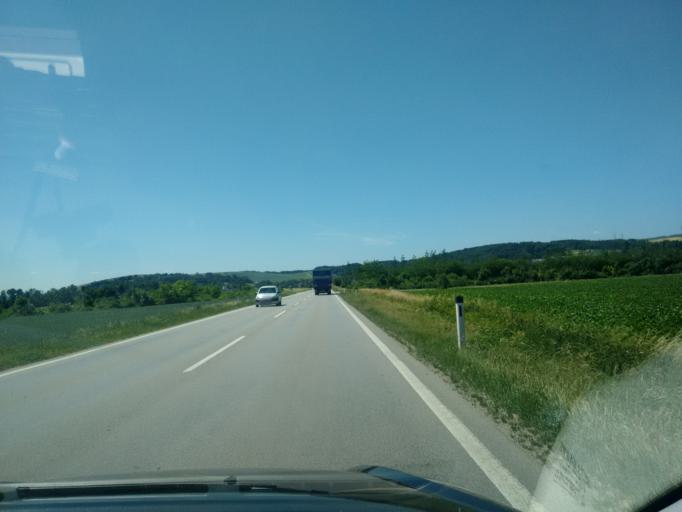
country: AT
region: Lower Austria
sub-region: Politischer Bezirk Sankt Polten
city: Hafnerbach
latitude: 48.1978
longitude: 15.4766
